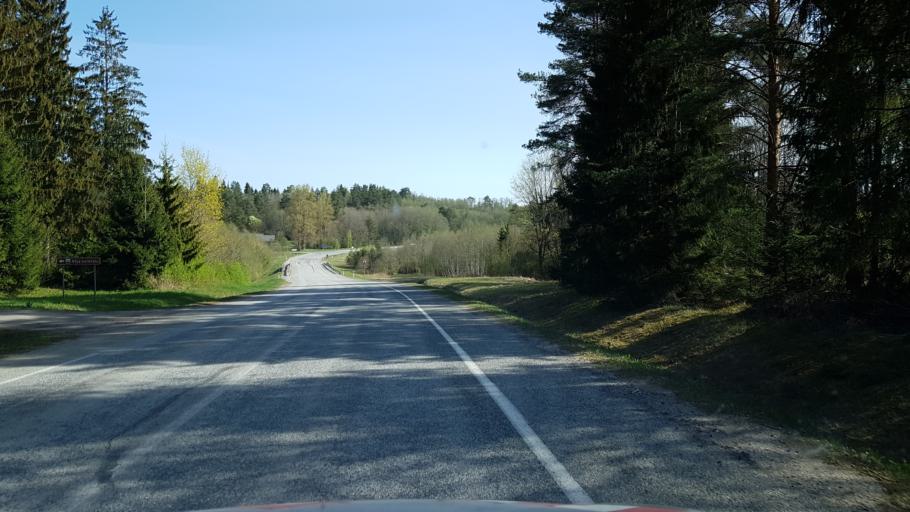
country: EE
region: Viljandimaa
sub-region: Abja vald
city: Abja-Paluoja
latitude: 58.1366
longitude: 25.3695
